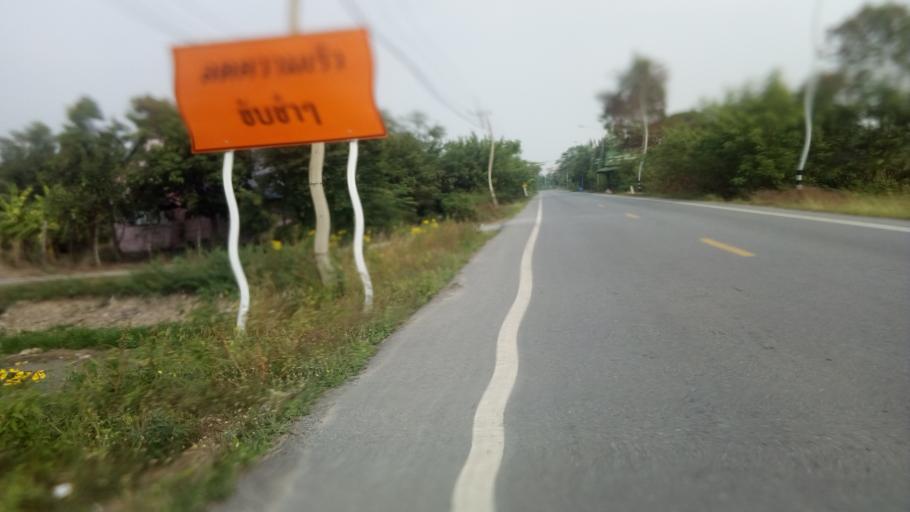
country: TH
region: Pathum Thani
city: Ban Rangsit
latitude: 14.0318
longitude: 100.8244
